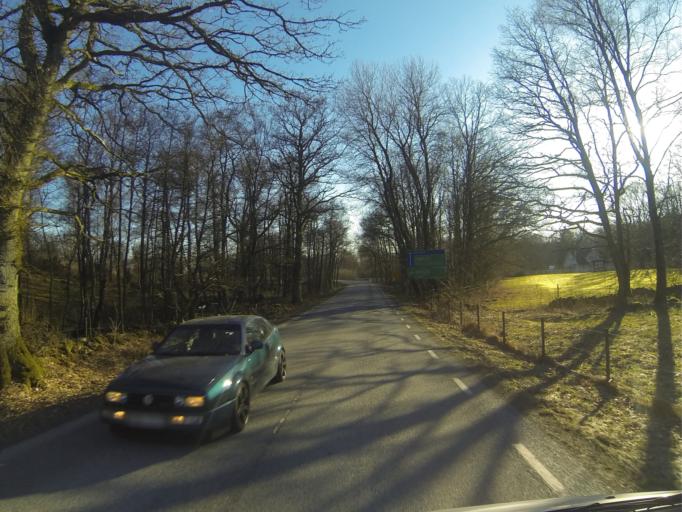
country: SE
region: Skane
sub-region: Horby Kommun
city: Hoerby
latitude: 55.8693
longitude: 13.6636
